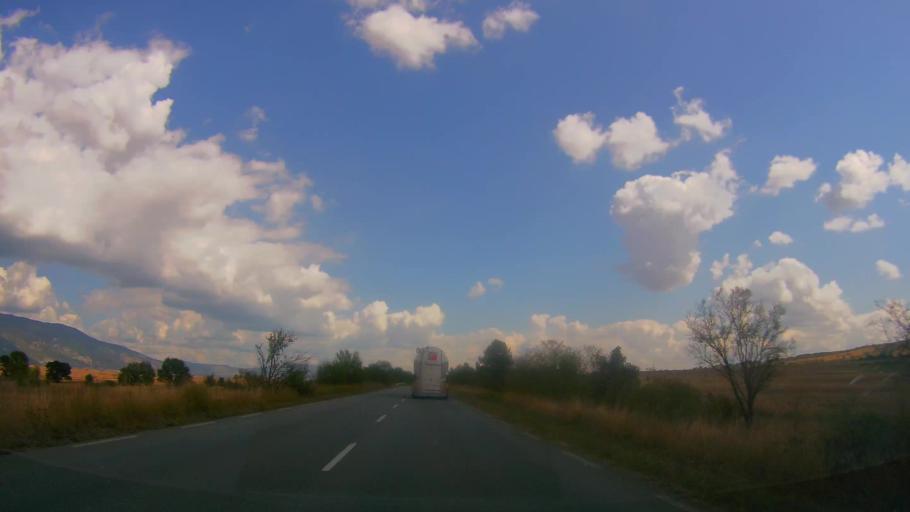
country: BG
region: Sliven
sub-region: Obshtina Tvurditsa
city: Tvurditsa
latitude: 42.6574
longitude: 25.9153
